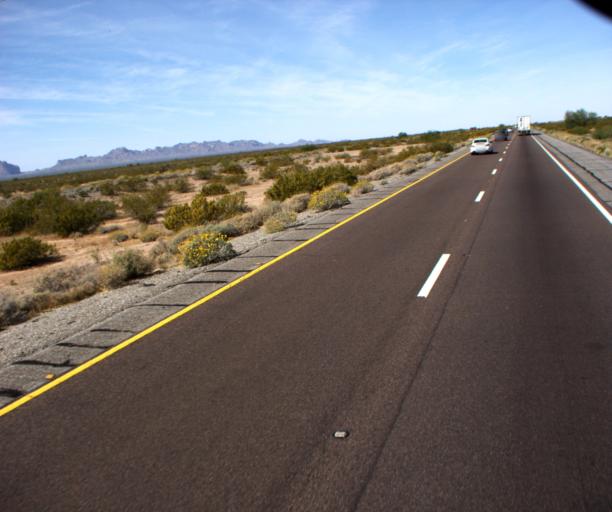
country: US
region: Arizona
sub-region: La Paz County
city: Salome
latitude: 33.5493
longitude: -113.2216
